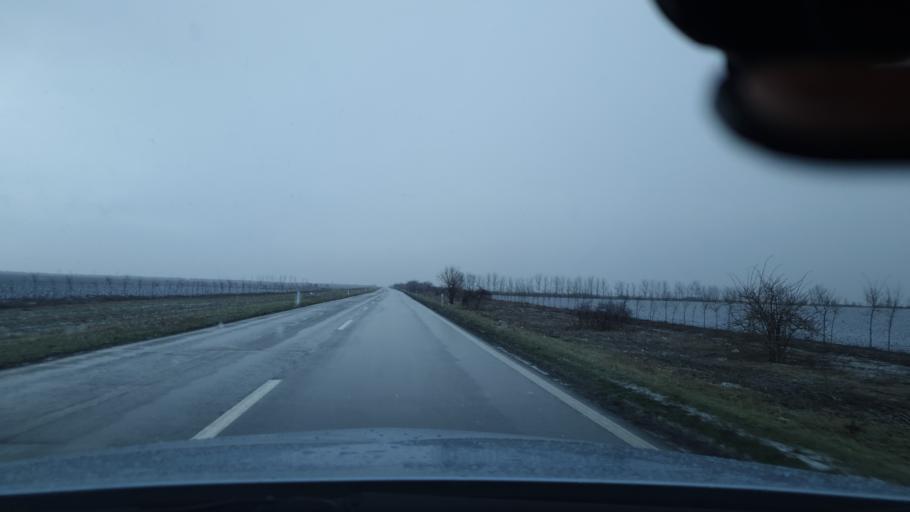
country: RS
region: Autonomna Pokrajina Vojvodina
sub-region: Juznobanatski Okrug
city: Pancevo
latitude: 44.8555
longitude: 20.7574
